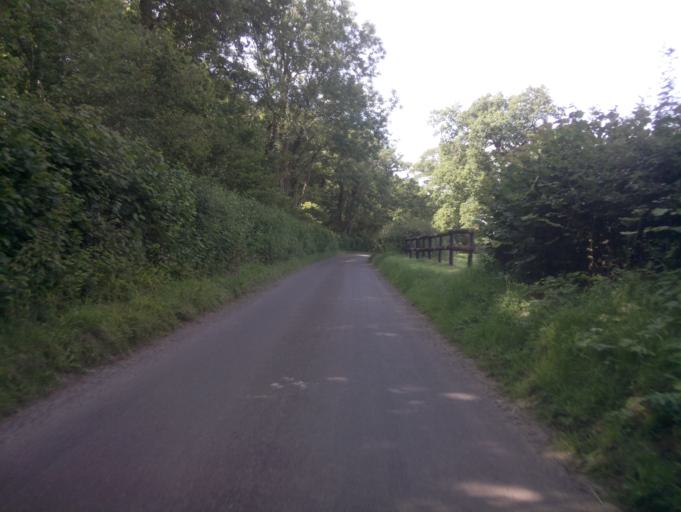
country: GB
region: England
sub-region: Wiltshire
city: Nettleton
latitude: 51.4971
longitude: -2.2672
